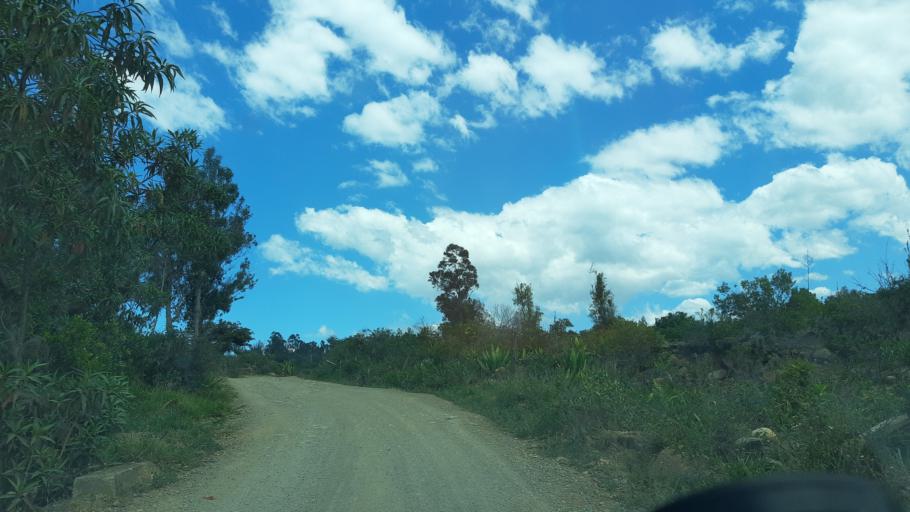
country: CO
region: Boyaca
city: Villa de Leiva
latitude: 5.6731
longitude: -73.5709
